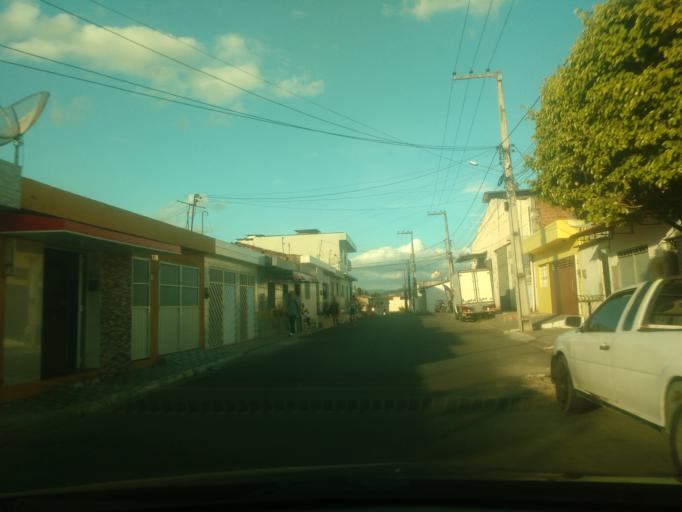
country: BR
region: Alagoas
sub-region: Uniao Dos Palmares
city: Uniao dos Palmares
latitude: -9.1576
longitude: -36.0285
